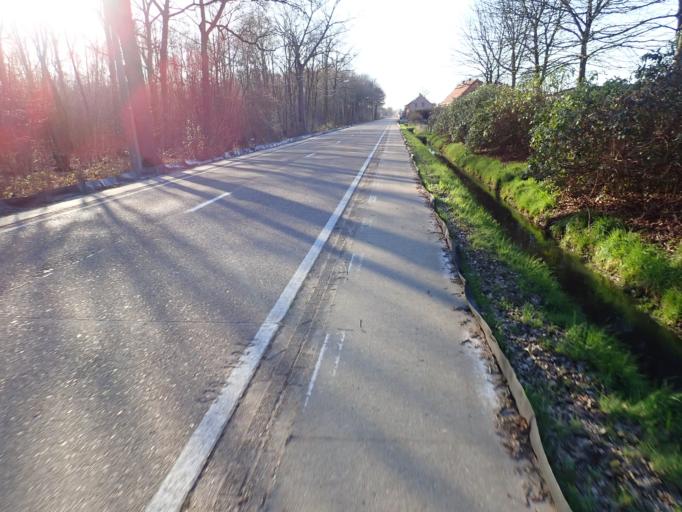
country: BE
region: Flanders
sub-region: Provincie Antwerpen
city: Herenthout
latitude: 51.1456
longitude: 4.7271
